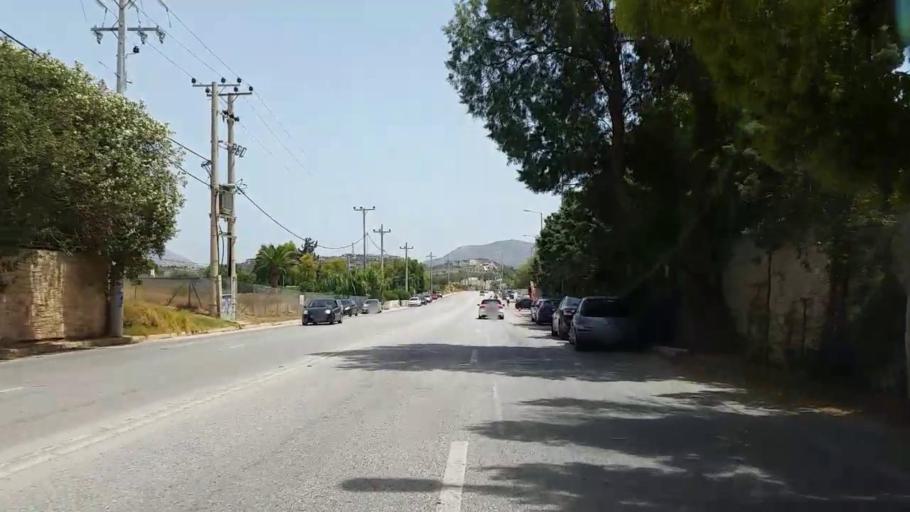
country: GR
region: Attica
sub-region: Nomarchia Anatolikis Attikis
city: Agios Dimitrios Kropias
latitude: 37.7937
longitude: 23.8761
